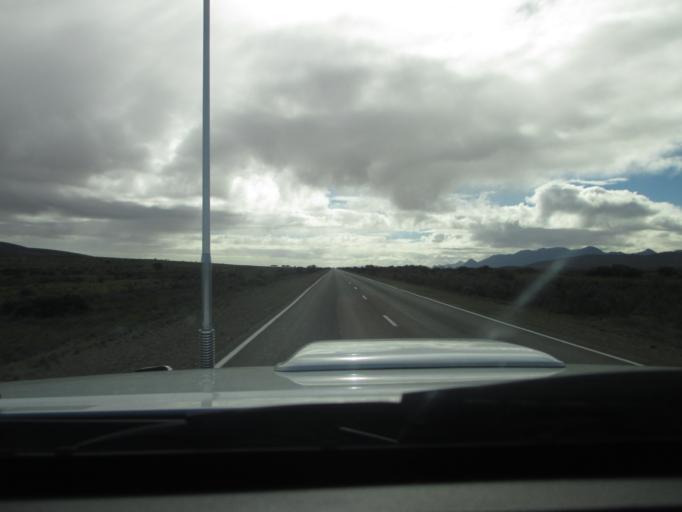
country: AU
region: South Australia
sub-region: Flinders Ranges
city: Quorn
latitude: -31.6423
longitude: 138.3836
